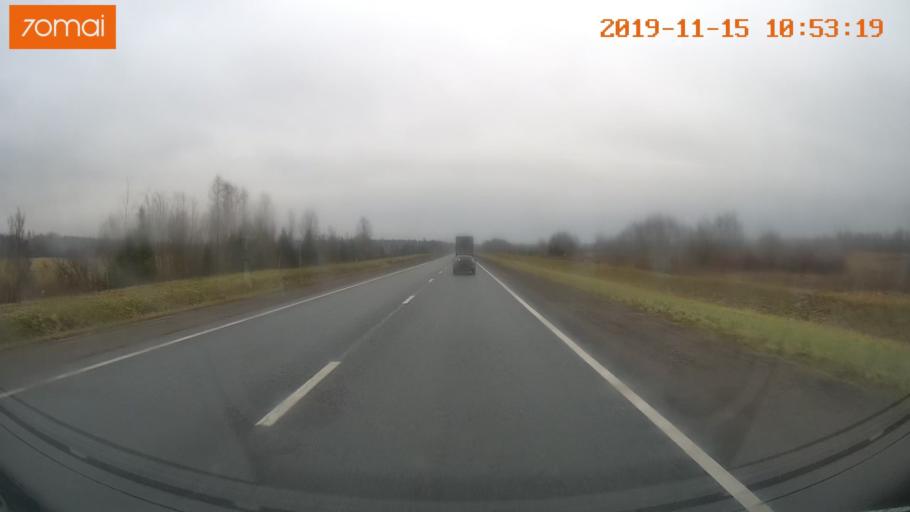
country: RU
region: Vologda
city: Chebsara
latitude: 59.1699
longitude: 38.7520
